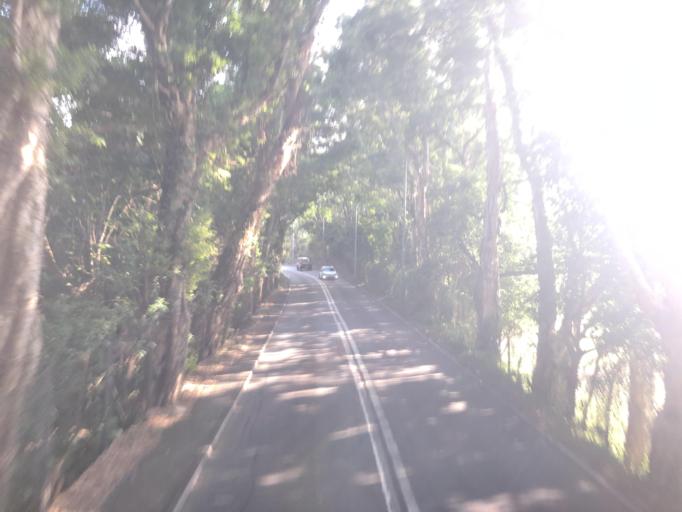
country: HK
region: Tai Po
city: Tai Po
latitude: 22.4942
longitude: 114.1203
